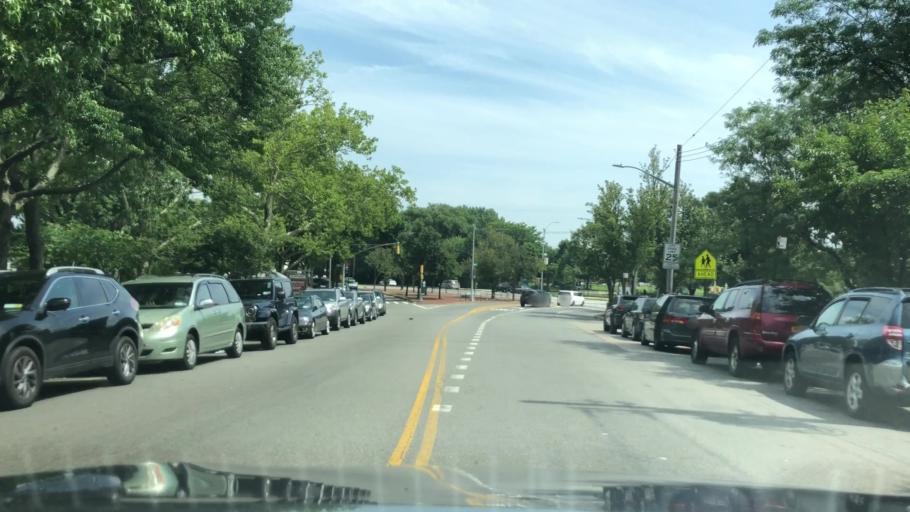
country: US
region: New York
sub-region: Queens County
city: Jamaica
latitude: 40.6739
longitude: -73.7887
